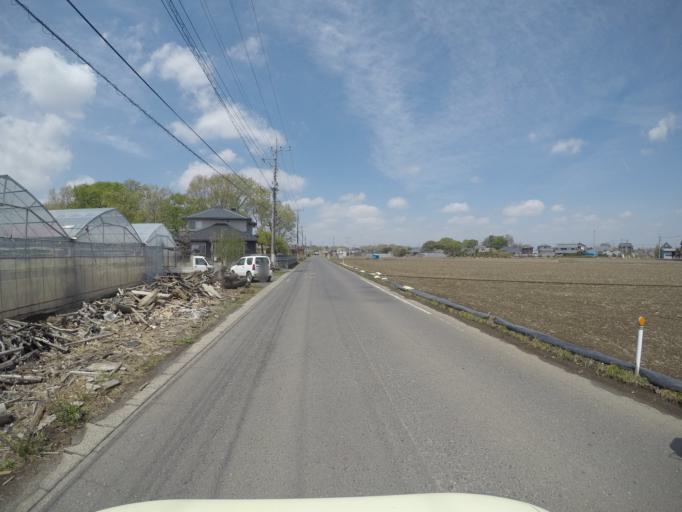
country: JP
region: Ibaraki
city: Shimodate
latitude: 36.3173
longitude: 140.0222
